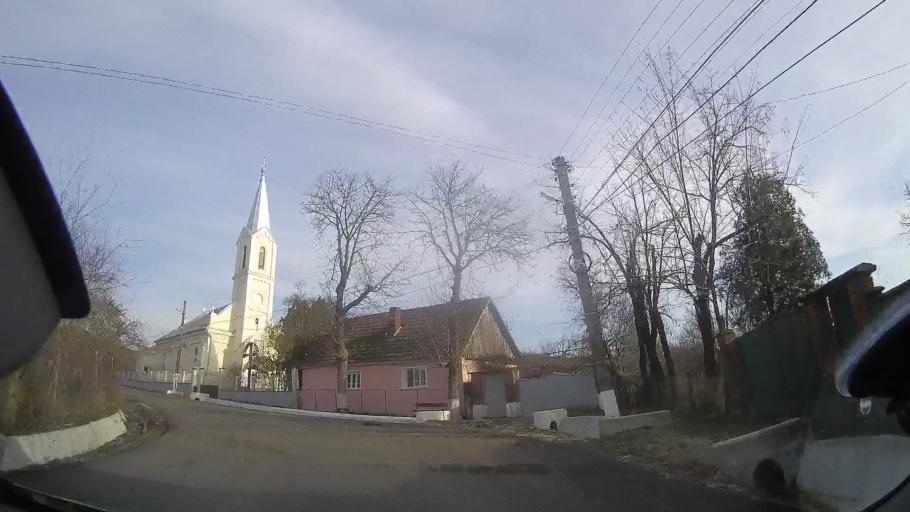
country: RO
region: Bihor
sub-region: Comuna Sarbi
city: Burzuc
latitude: 47.1763
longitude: 22.1501
